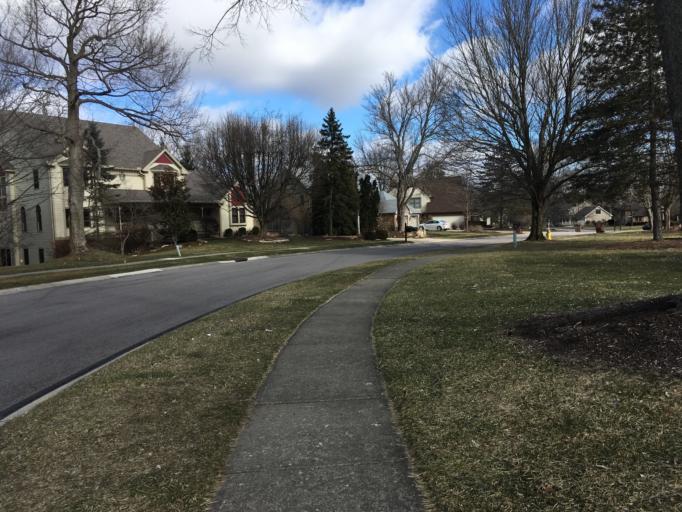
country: US
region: Ohio
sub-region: Montgomery County
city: Centerville
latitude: 39.5953
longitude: -84.1507
